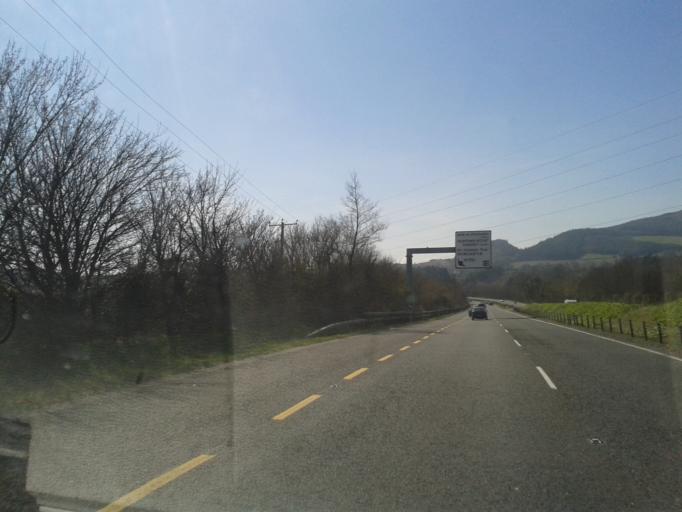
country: IE
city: Kilquade
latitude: 53.0789
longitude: -6.0901
